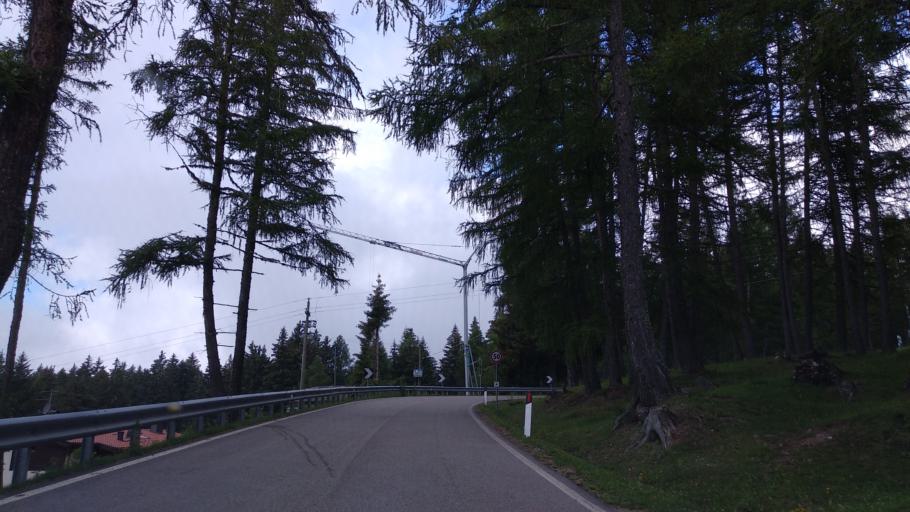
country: IT
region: Trentino-Alto Adige
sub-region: Bolzano
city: Avelengo
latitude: 46.6609
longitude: 11.2331
